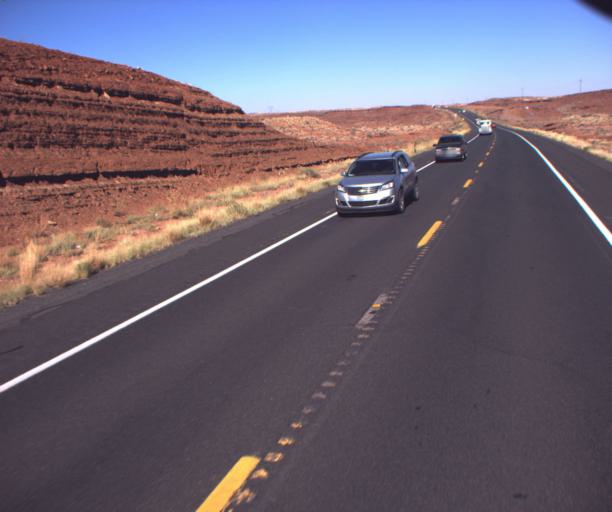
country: US
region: Arizona
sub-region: Coconino County
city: Tuba City
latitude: 35.7862
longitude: -111.4524
